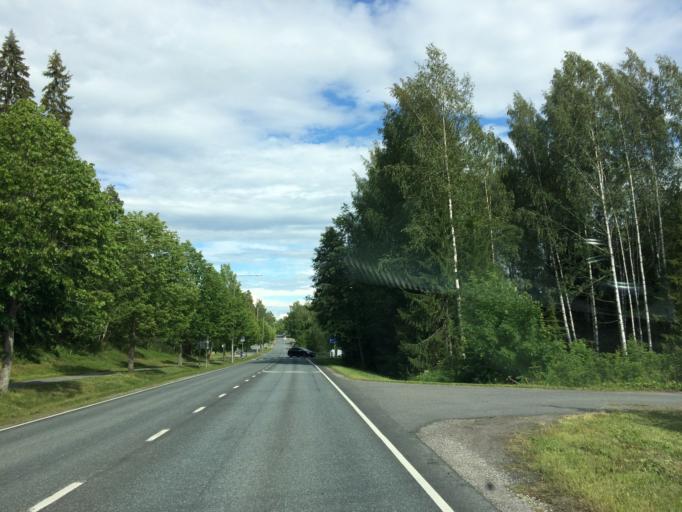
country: FI
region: Haeme
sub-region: Haemeenlinna
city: Turenki
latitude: 60.9204
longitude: 24.6165
